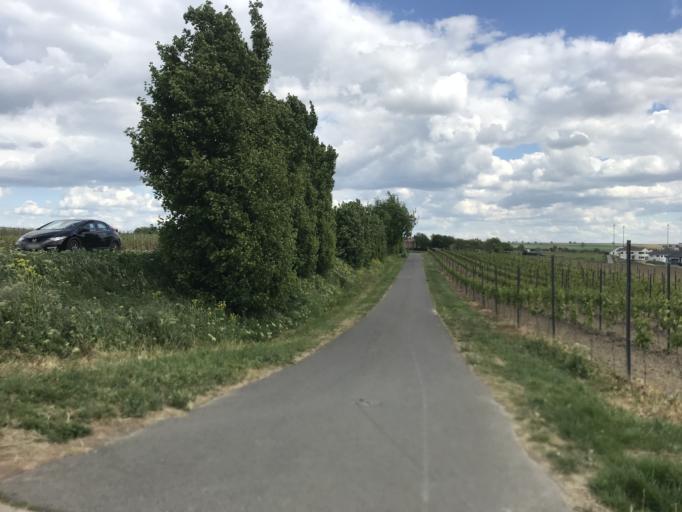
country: DE
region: Rheinland-Pfalz
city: Lorzweiler
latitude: 49.9021
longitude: 8.2858
